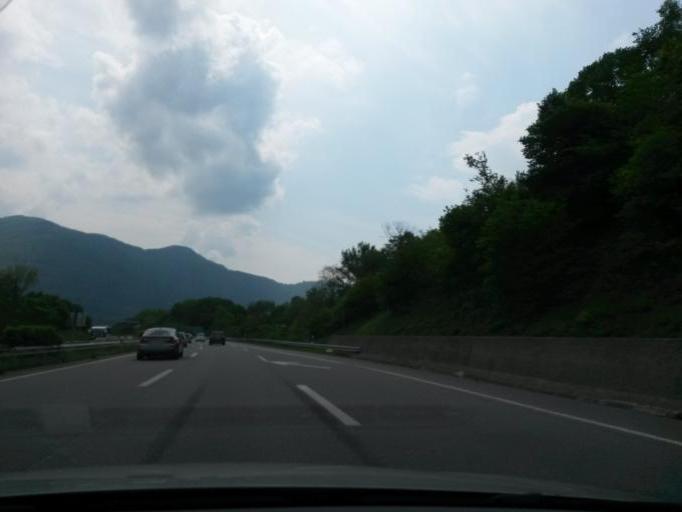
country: CH
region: Ticino
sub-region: Bellinzona District
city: Cadenazzo
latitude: 46.1248
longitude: 8.9189
